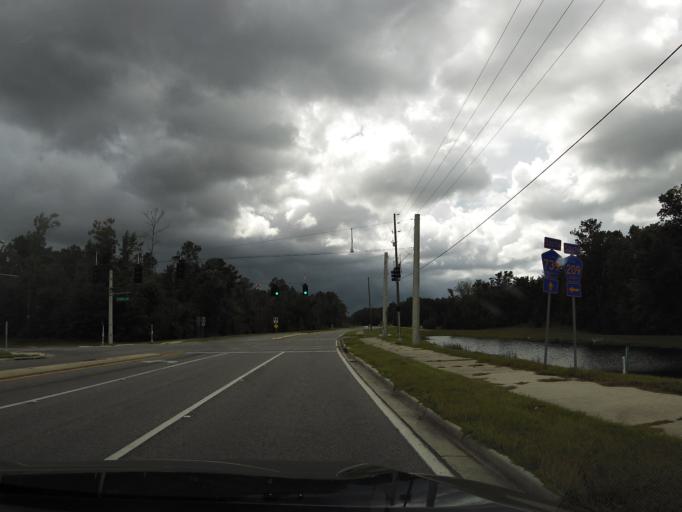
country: US
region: Florida
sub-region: Clay County
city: Asbury Lake
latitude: 30.0779
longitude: -81.8093
